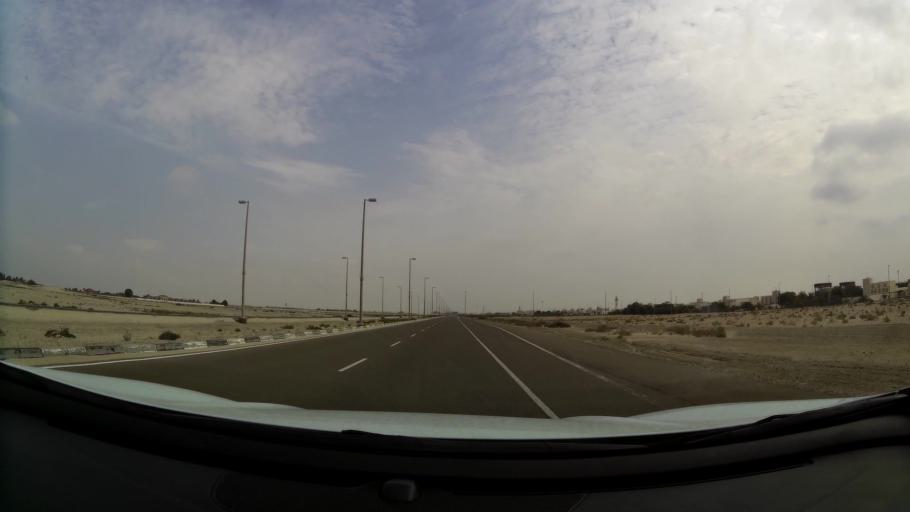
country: AE
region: Abu Dhabi
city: Abu Dhabi
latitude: 24.6462
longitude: 54.6706
